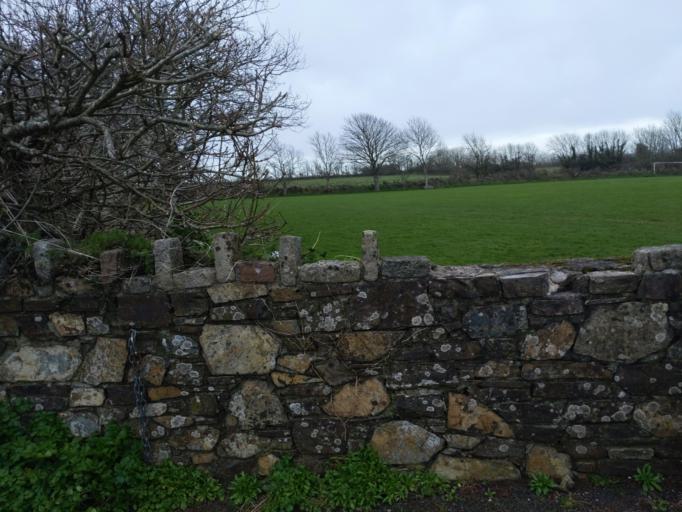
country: GB
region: England
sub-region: Devon
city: Yealmpton
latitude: 50.3239
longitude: -4.0304
